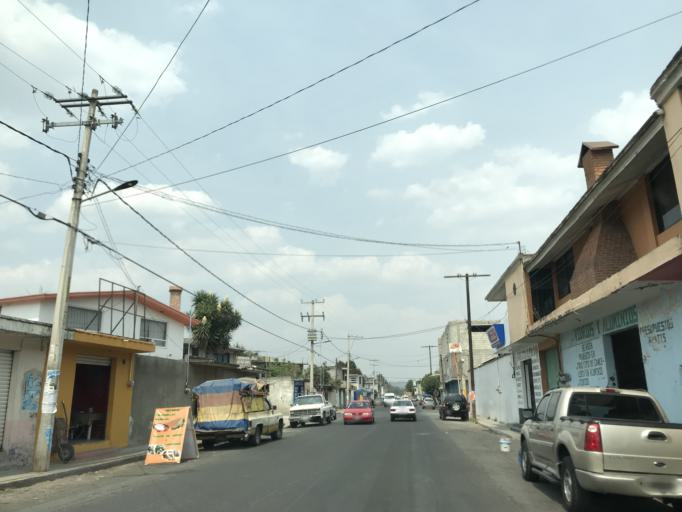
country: MX
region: Tlaxcala
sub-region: Panotla
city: Fraccionamiento la Virgen
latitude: 19.3185
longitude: -98.3135
